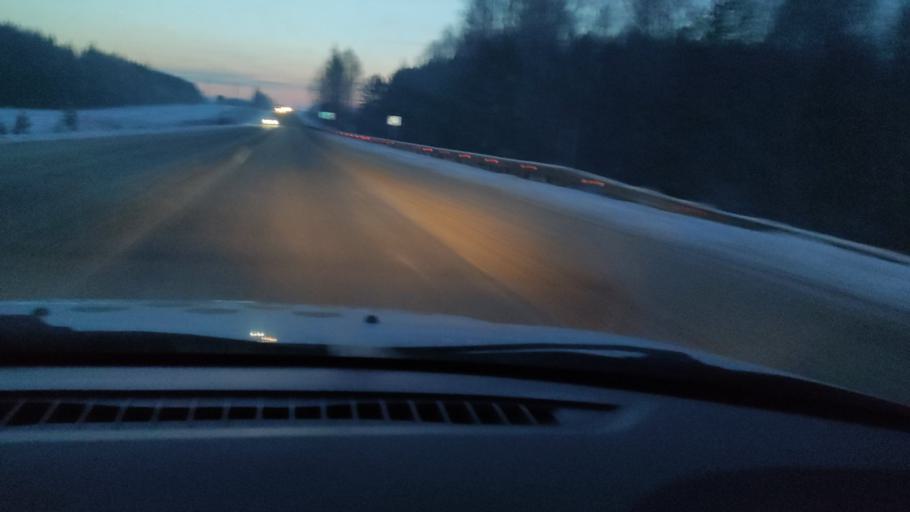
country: RU
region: Perm
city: Kungur
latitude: 57.4090
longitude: 56.9037
